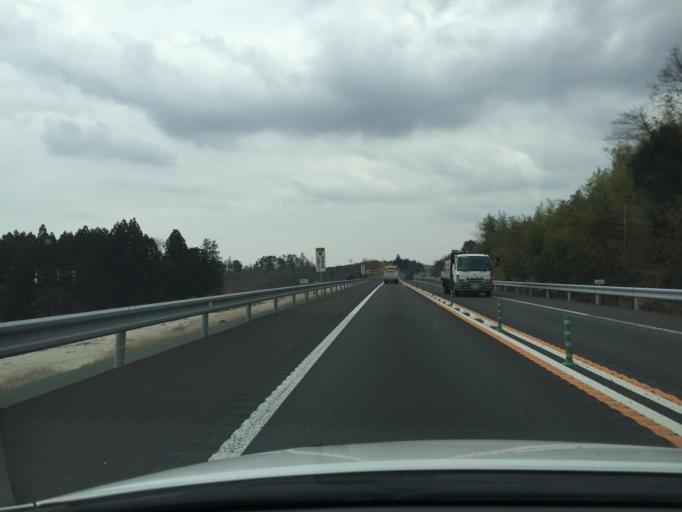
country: JP
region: Miyagi
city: Marumori
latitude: 37.8138
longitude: 140.8792
